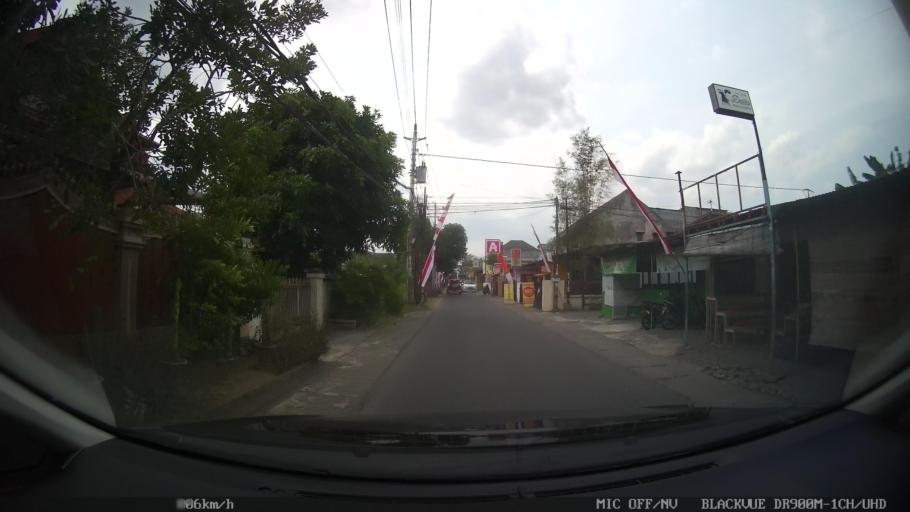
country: ID
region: Daerah Istimewa Yogyakarta
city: Yogyakarta
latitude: -7.7913
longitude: 110.3984
